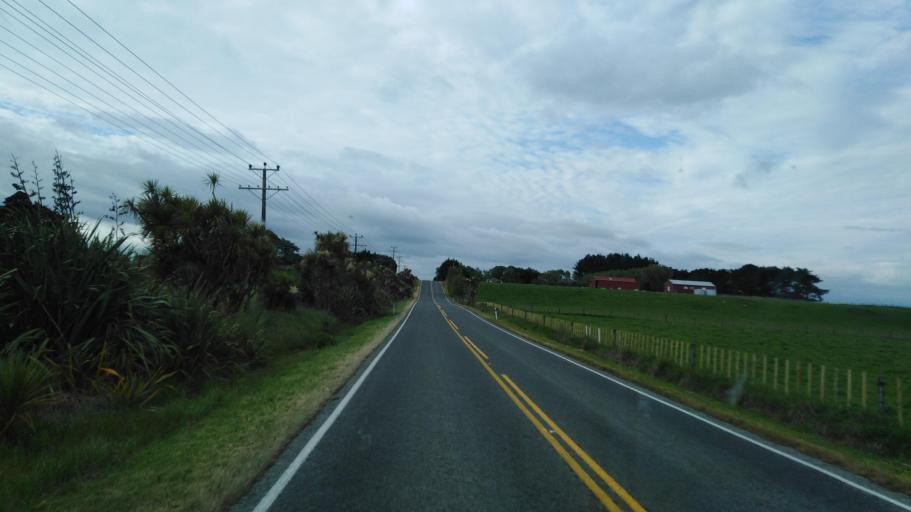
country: NZ
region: Manawatu-Wanganui
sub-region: Rangitikei District
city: Bulls
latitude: -40.1191
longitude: 175.3562
